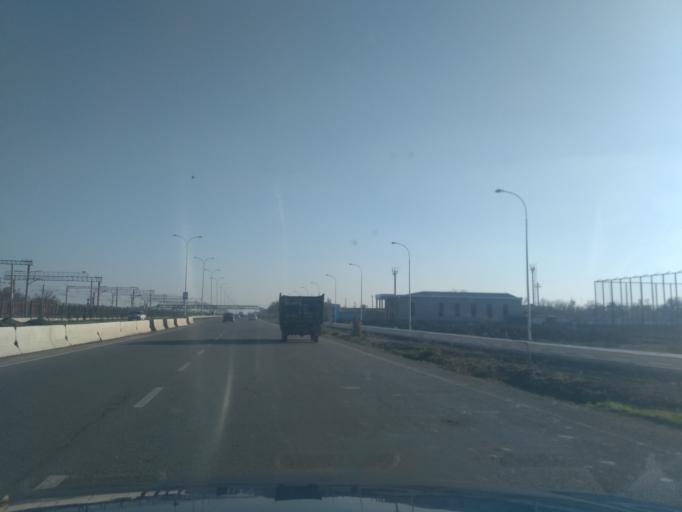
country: UZ
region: Sirdaryo
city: Guliston
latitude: 40.5035
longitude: 68.7617
